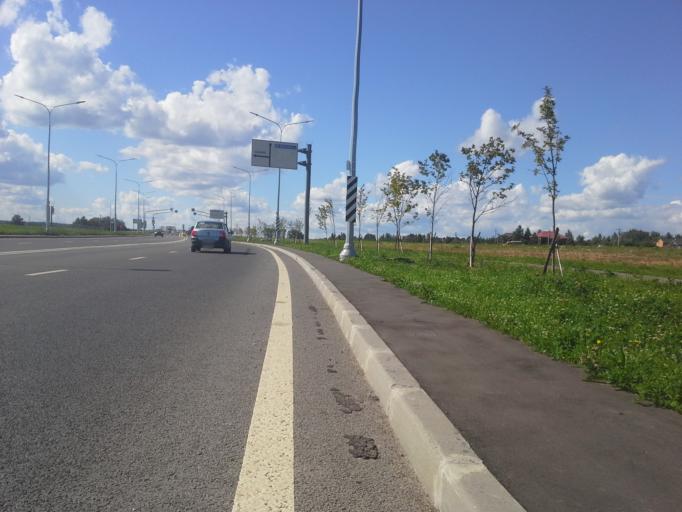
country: RU
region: Moskovskaya
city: Kokoshkino
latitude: 55.5869
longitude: 37.1613
